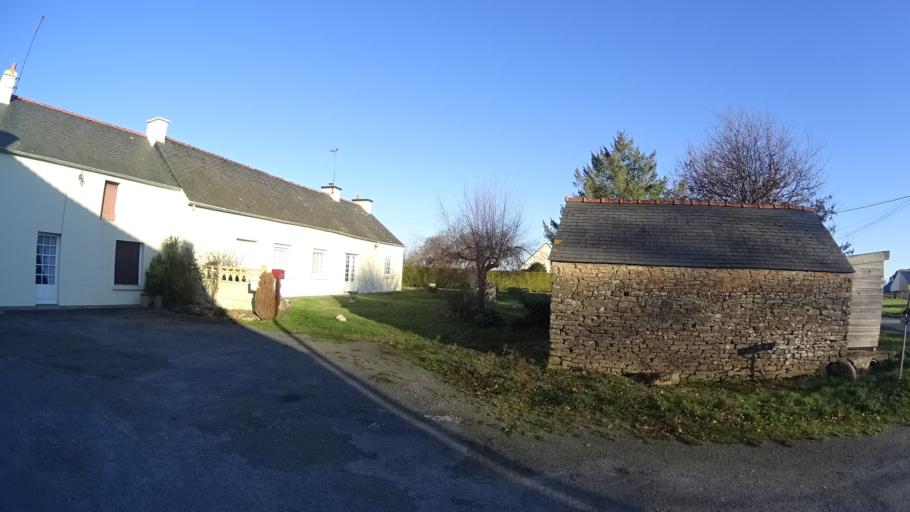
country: FR
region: Brittany
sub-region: Departement du Morbihan
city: Allaire
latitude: 47.6515
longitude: -2.1595
